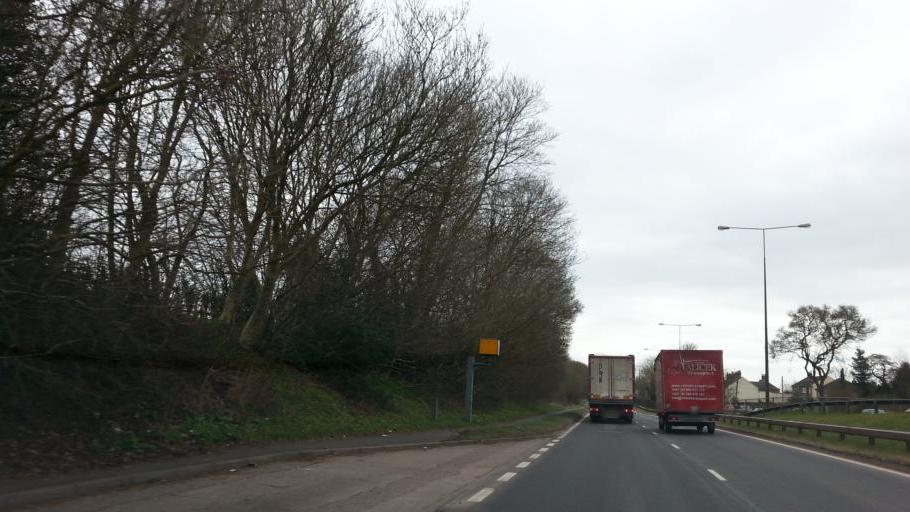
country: GB
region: England
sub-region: Staffordshire
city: Stone
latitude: 52.9010
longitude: -2.1564
